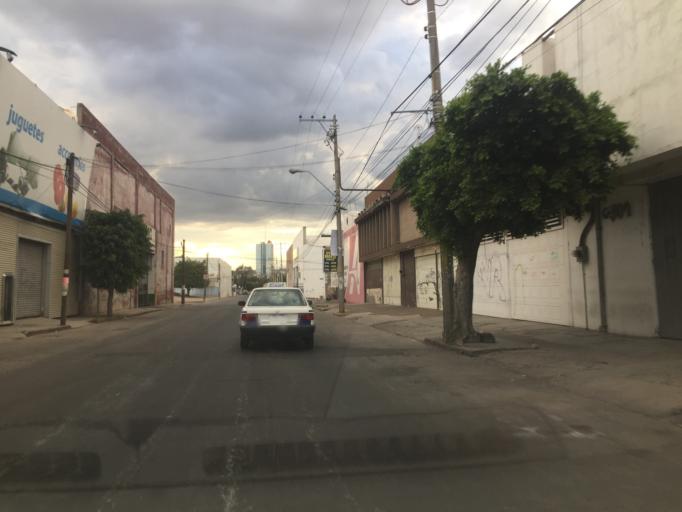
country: MX
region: Guanajuato
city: Leon
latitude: 21.1424
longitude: -101.6821
